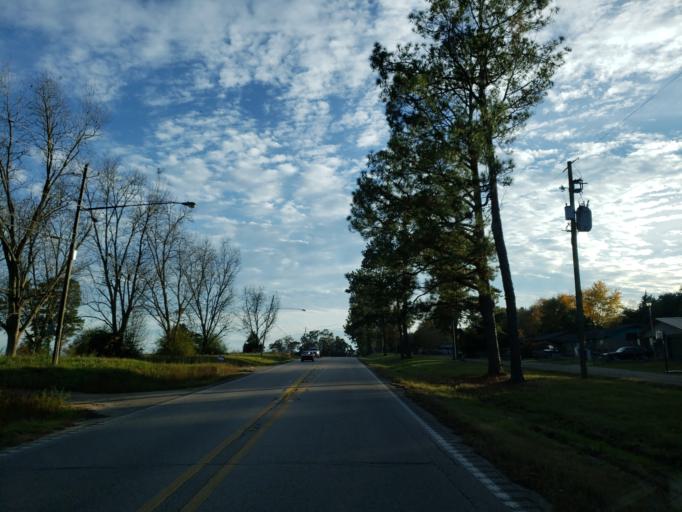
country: US
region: Mississippi
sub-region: Lamar County
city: Purvis
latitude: 31.1338
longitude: -89.4059
